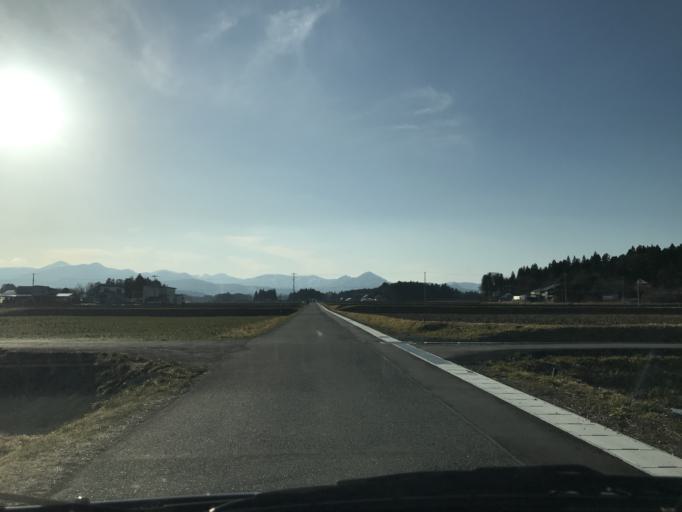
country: JP
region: Iwate
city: Kitakami
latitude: 39.2282
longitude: 141.0751
